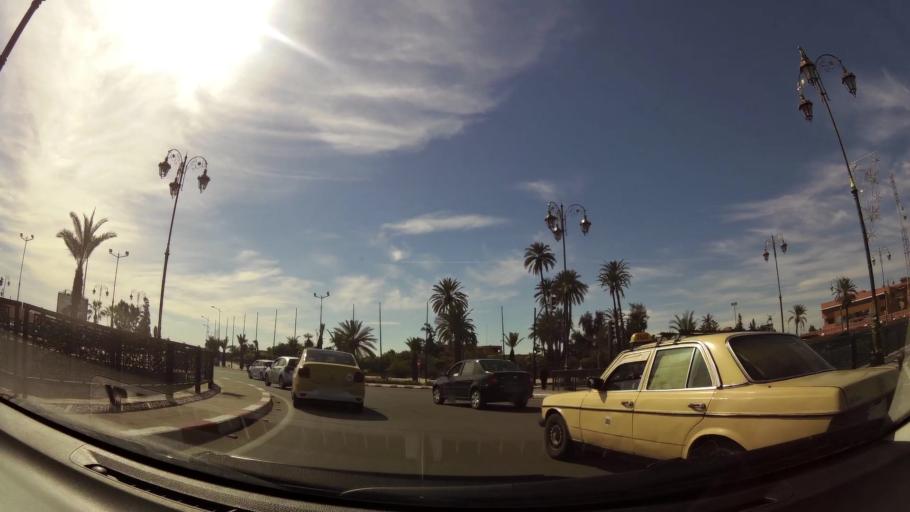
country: MA
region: Marrakech-Tensift-Al Haouz
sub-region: Marrakech
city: Marrakesh
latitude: 31.6449
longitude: -7.9874
